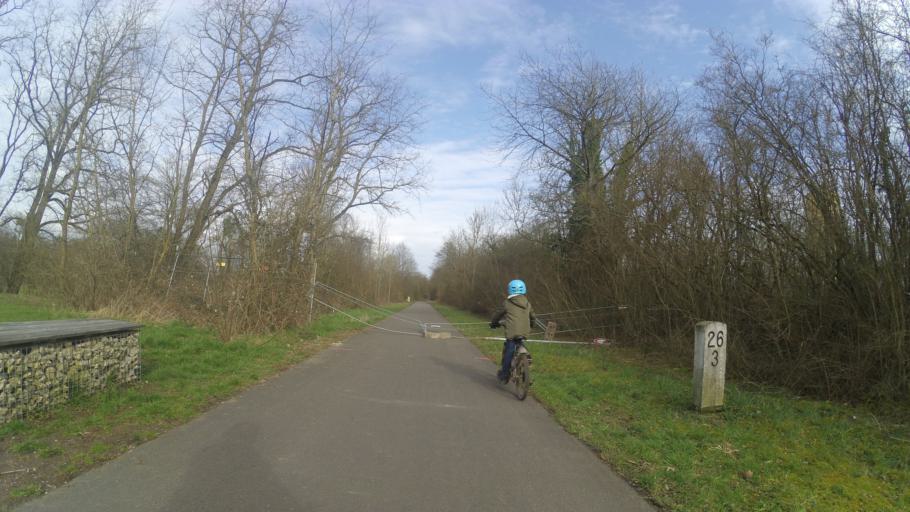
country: DE
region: Saarland
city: Gersheim
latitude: 49.1368
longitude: 7.1944
